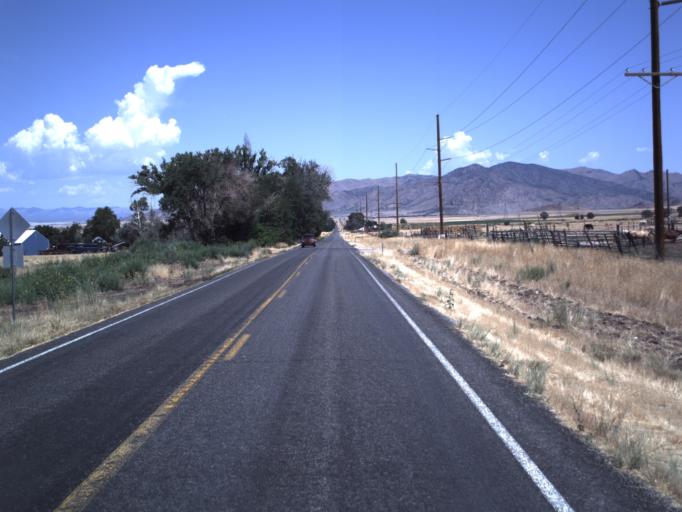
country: US
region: Utah
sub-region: Millard County
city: Delta
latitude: 39.4739
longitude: -112.2687
